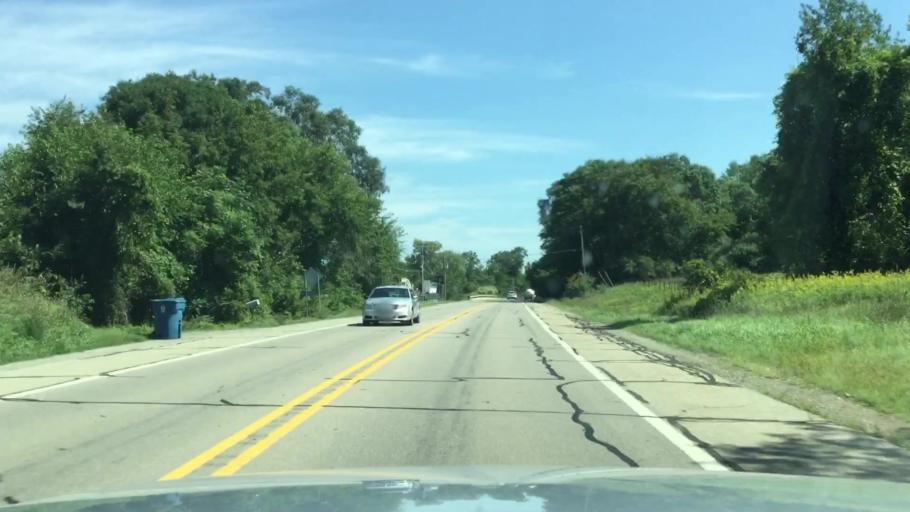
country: US
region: Michigan
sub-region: Washtenaw County
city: Manchester
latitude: 42.0658
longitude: -84.1062
